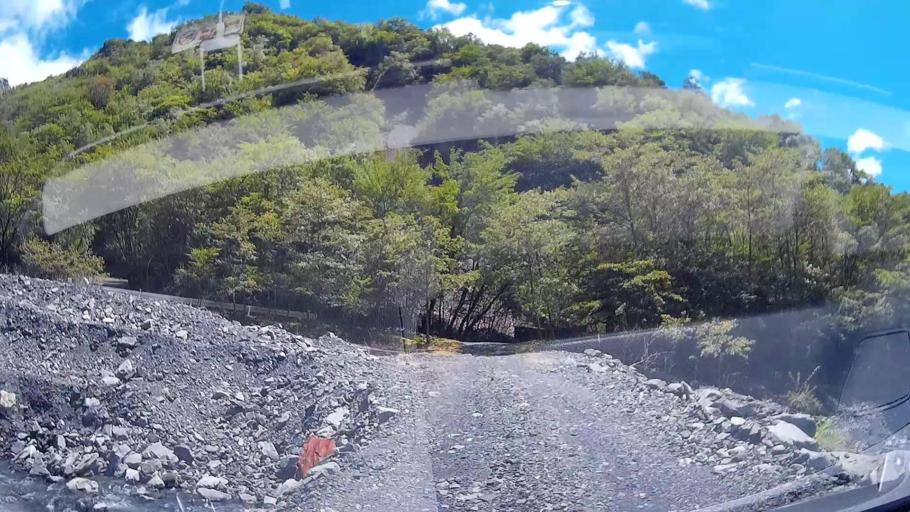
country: JP
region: Shizuoka
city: Fujinomiya
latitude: 35.3033
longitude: 138.3127
